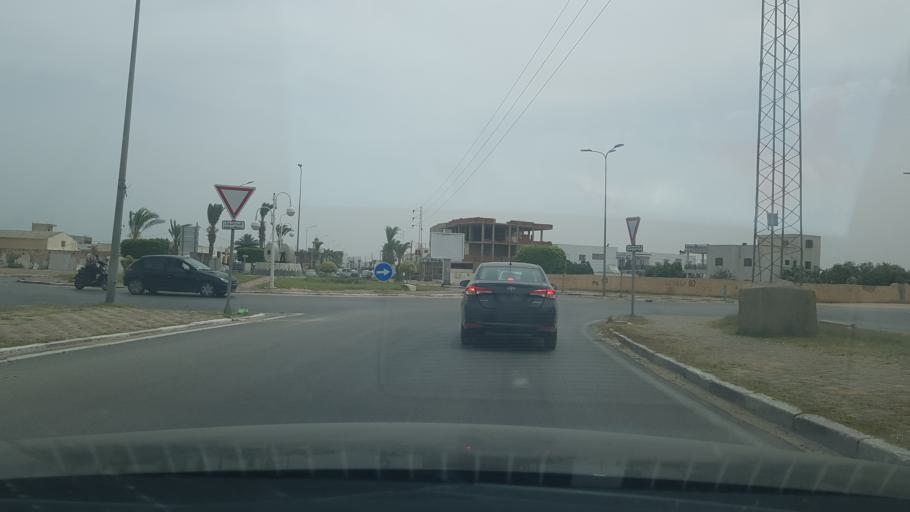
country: TN
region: Safaqis
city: Al Qarmadah
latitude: 34.8255
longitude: 10.7636
